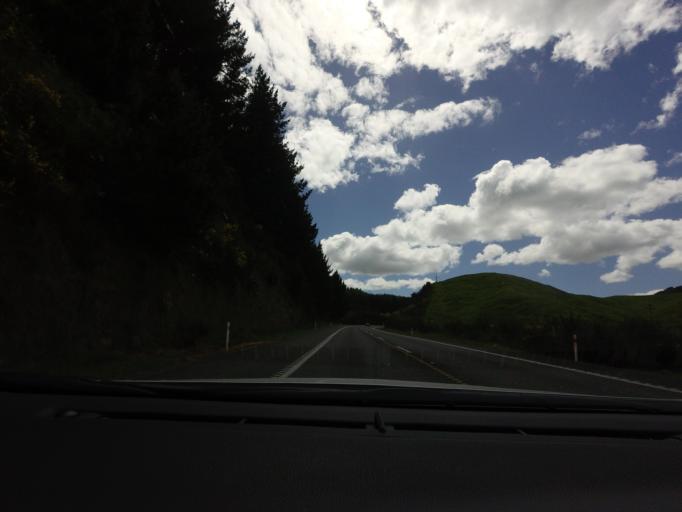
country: NZ
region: Bay of Plenty
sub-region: Rotorua District
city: Rotorua
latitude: -38.2879
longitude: 176.3501
